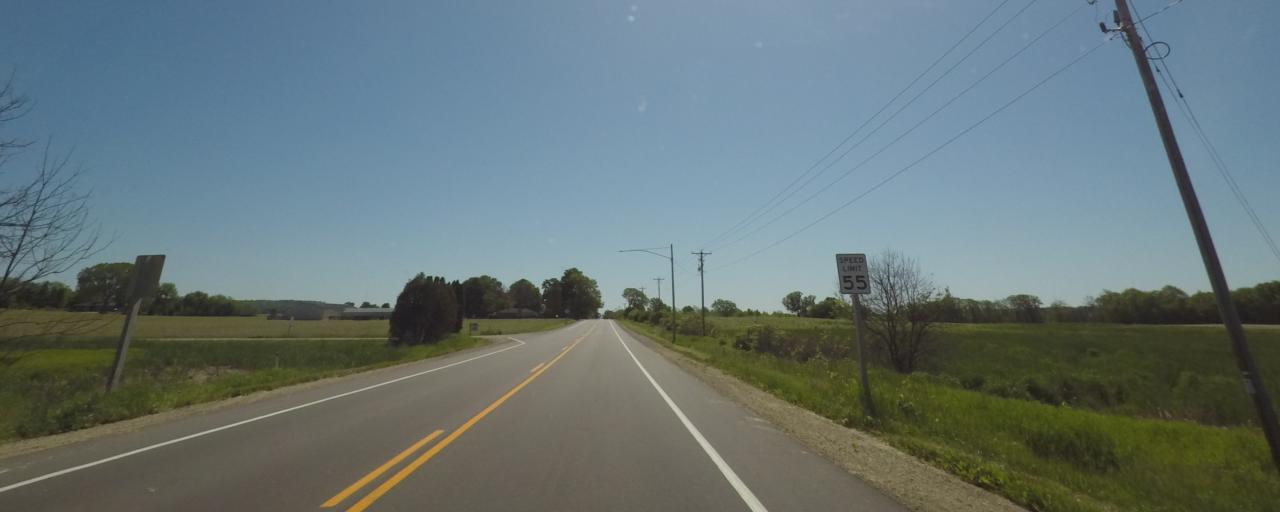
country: US
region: Wisconsin
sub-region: Dane County
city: Fitchburg
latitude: 42.9504
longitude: -89.4325
